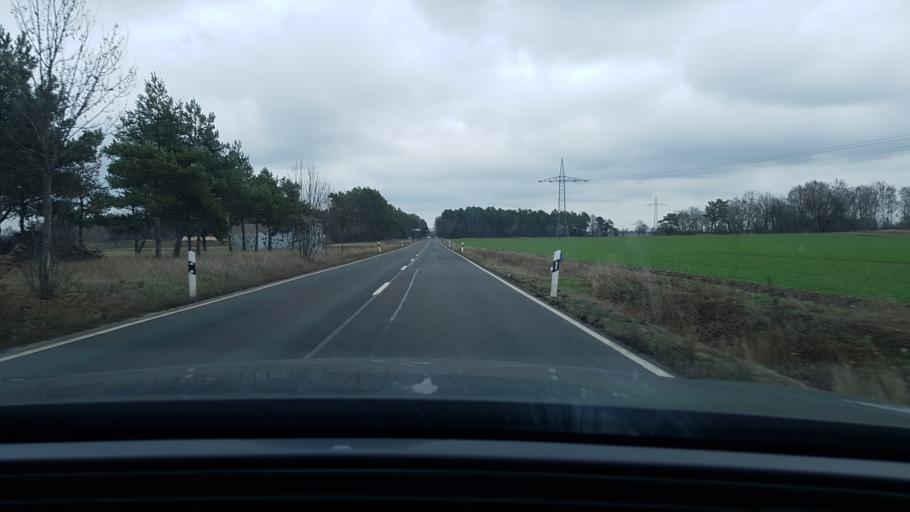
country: DE
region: Lower Saxony
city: Bahrdorf
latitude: 52.4177
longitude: 11.0502
